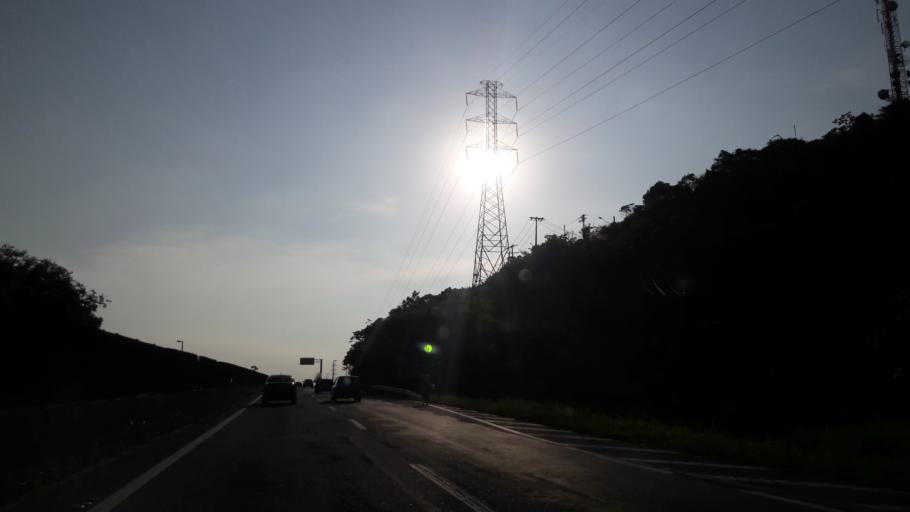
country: BR
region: Sao Paulo
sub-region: Mongagua
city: Mongagua
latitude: -24.0984
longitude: -46.6318
